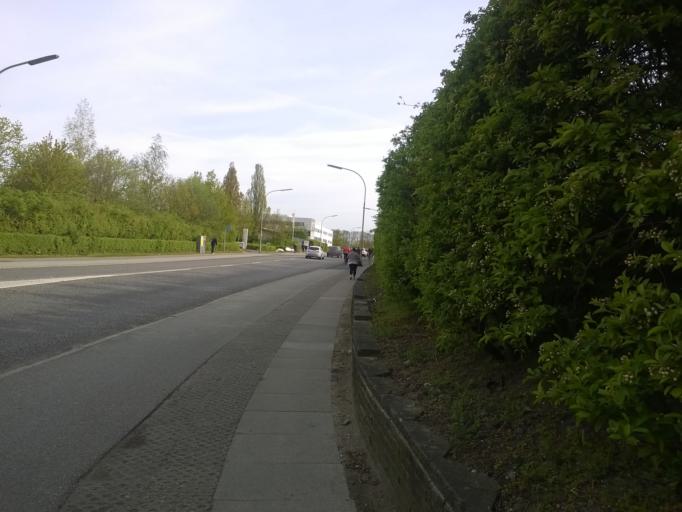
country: DK
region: Capital Region
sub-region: Ballerup Kommune
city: Ballerup
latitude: 55.7248
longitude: 12.3859
